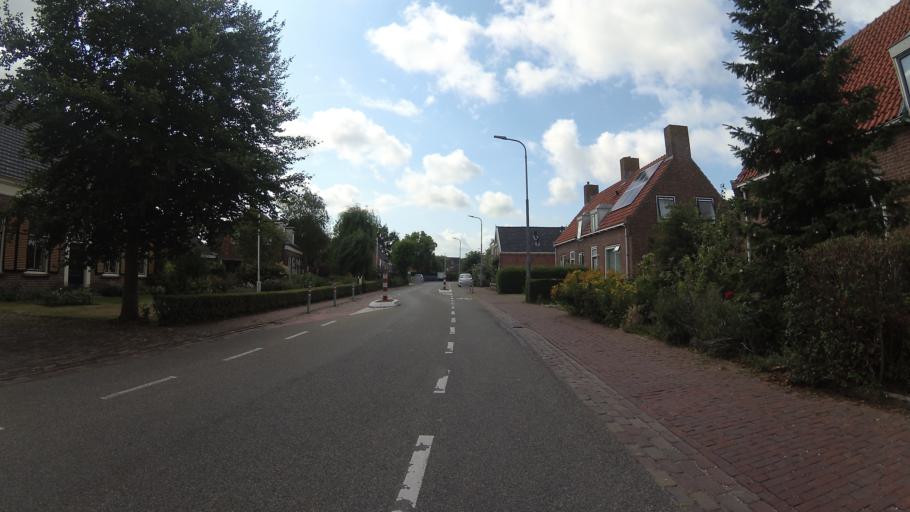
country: NL
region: Zeeland
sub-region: Gemeente Middelburg
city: Middelburg
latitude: 51.5518
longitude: 3.5972
